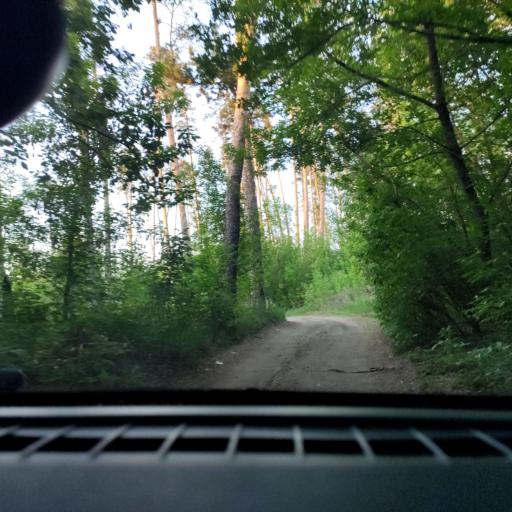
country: RU
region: Samara
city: Tol'yatti
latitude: 53.4775
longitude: 49.3712
